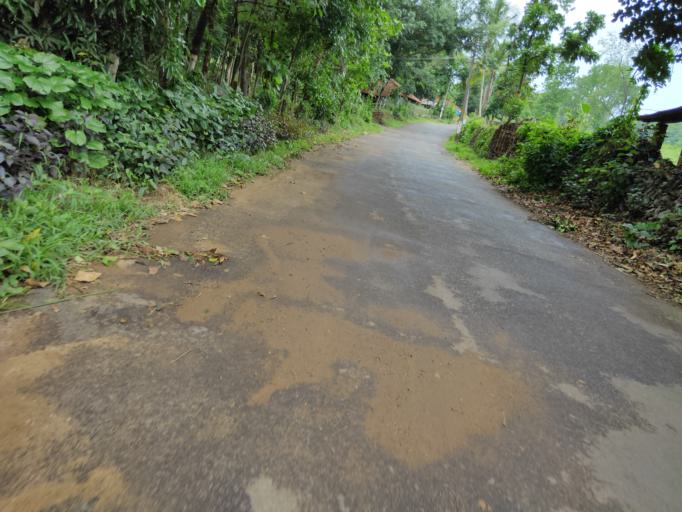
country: IN
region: Kerala
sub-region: Malappuram
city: Manjeri
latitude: 11.2360
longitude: 76.2477
